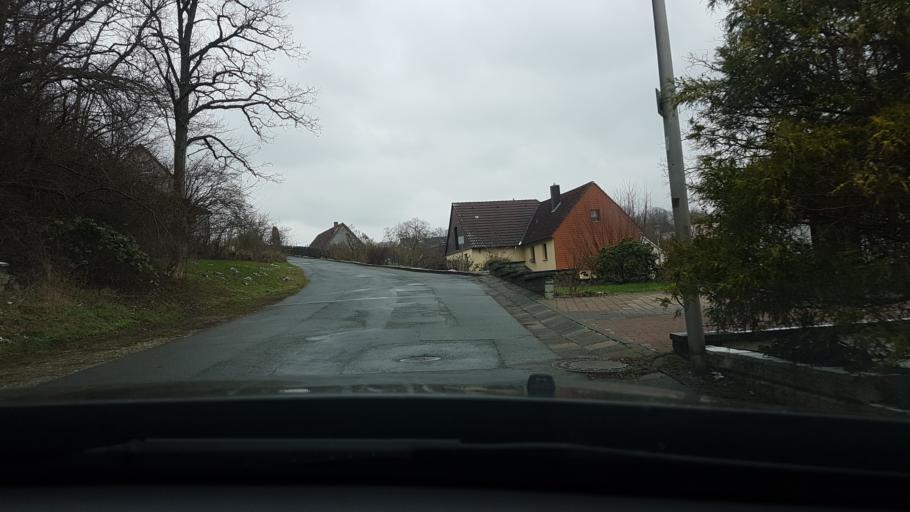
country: DE
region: Hesse
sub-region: Regierungsbezirk Kassel
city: Bad Arolsen
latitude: 51.4735
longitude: 9.0066
